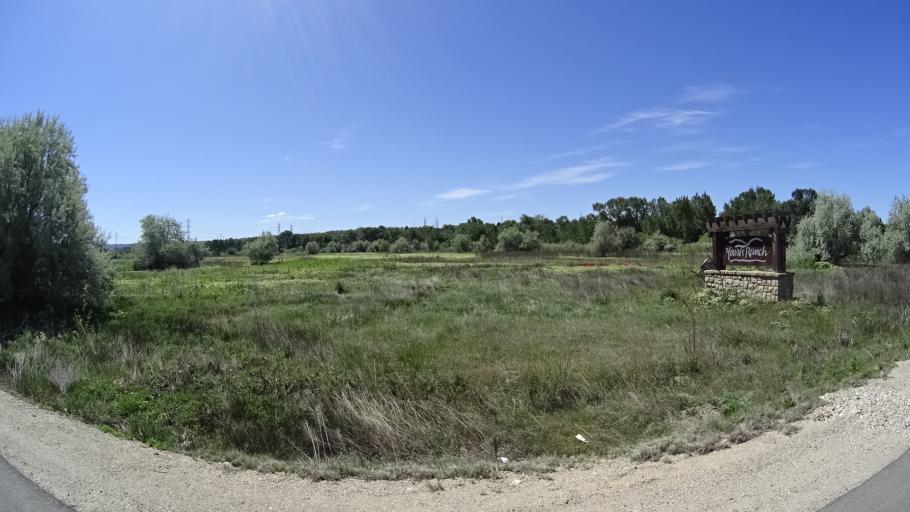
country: US
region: Idaho
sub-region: Ada County
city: Boise
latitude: 43.5666
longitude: -116.1297
